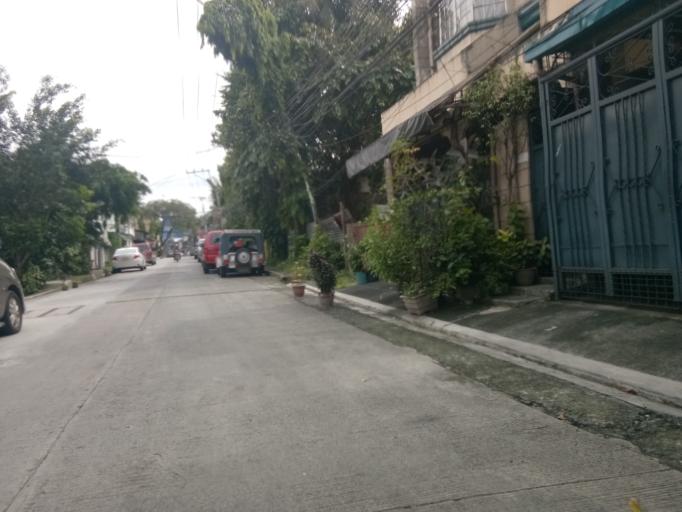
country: PH
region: Metro Manila
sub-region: San Juan
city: San Juan
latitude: 14.6120
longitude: 121.0514
